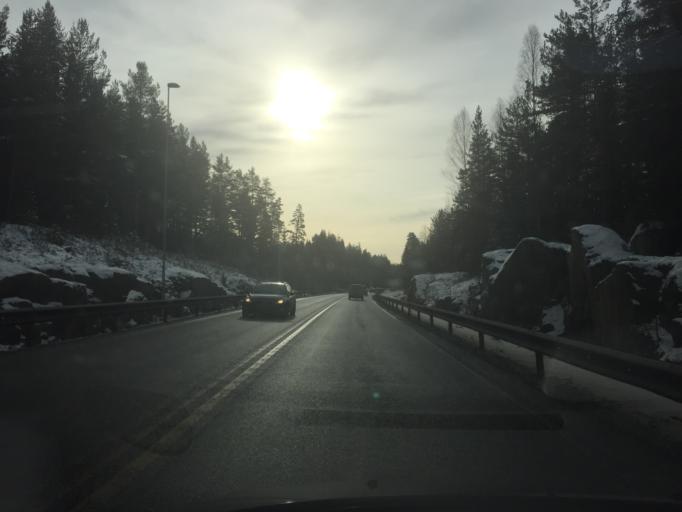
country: NO
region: Hedmark
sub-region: Stange
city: Stange
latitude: 60.7255
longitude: 11.2915
